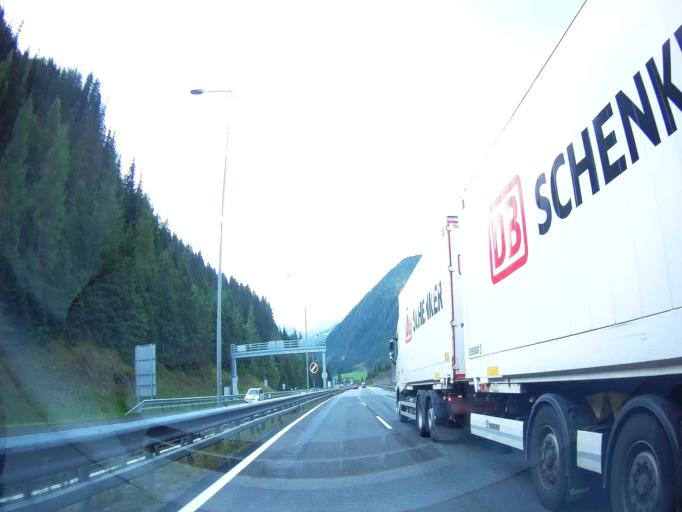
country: AT
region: Salzburg
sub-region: Politischer Bezirk Sankt Johann im Pongau
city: Flachau
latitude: 47.3412
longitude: 13.3958
